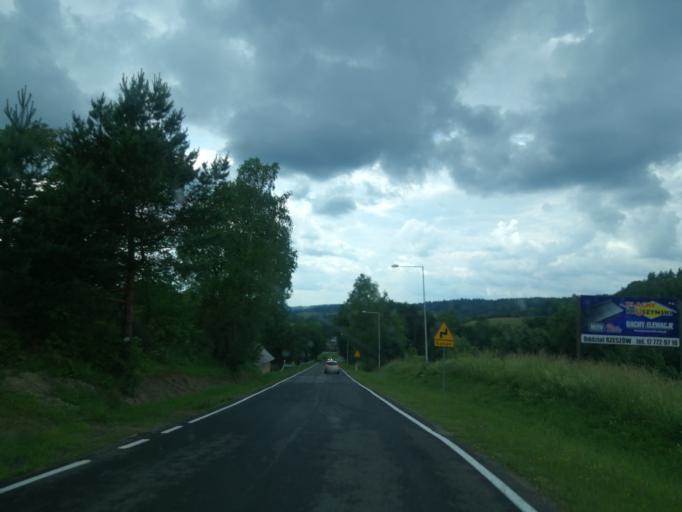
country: PL
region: Subcarpathian Voivodeship
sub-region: Powiat leski
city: Olszanica
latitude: 49.4415
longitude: 22.4525
